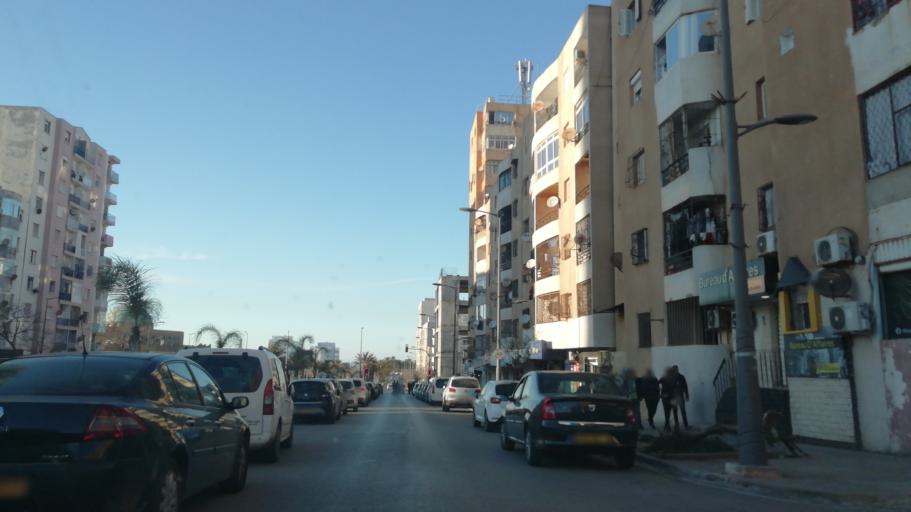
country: DZ
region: Oran
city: Bir el Djir
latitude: 35.7220
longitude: -0.5919
